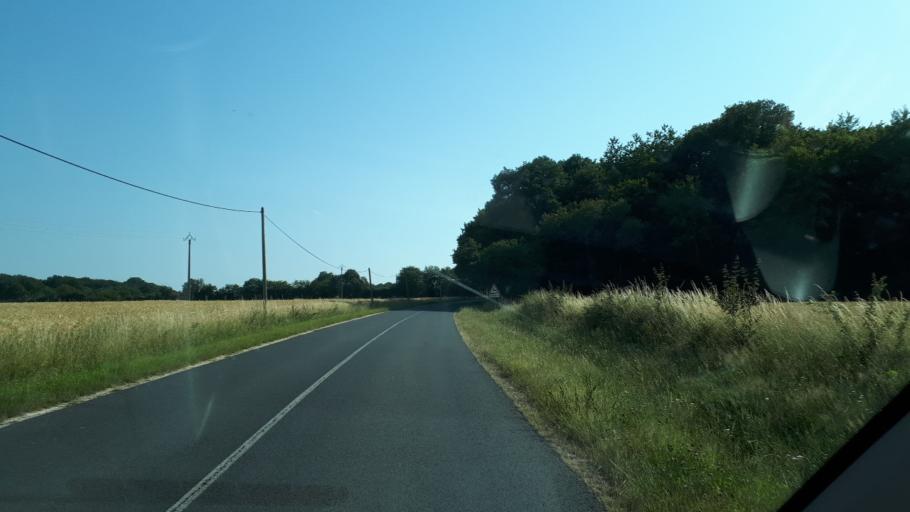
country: FR
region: Centre
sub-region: Departement du Loir-et-Cher
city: Droue
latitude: 48.0227
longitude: 1.0627
